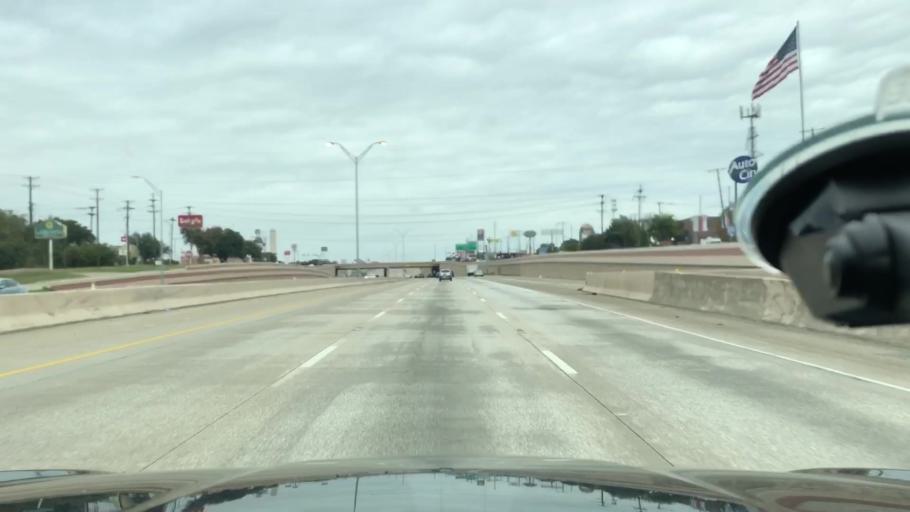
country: US
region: Texas
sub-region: Dallas County
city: DeSoto
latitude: 32.5998
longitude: -96.8224
